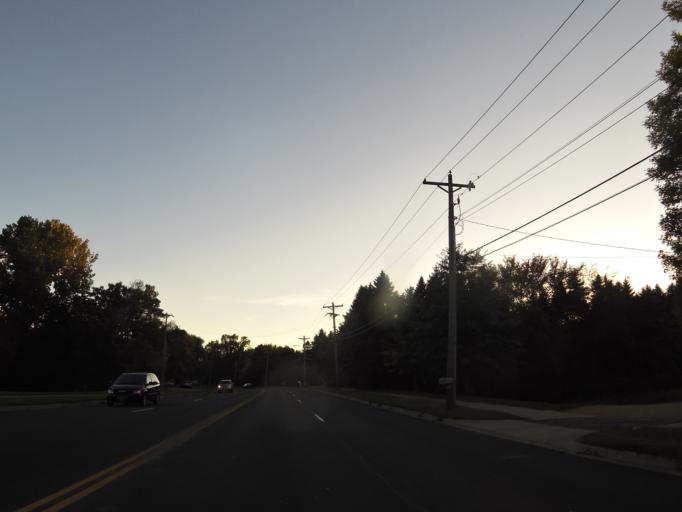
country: US
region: Minnesota
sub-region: Dakota County
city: Inver Grove Heights
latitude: 44.8636
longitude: -93.0436
